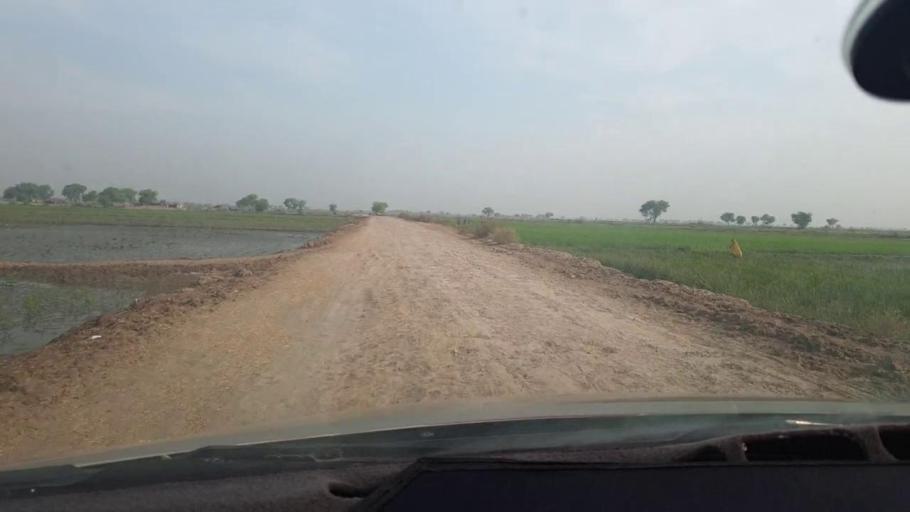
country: PK
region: Balochistan
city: Jhatpat
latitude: 28.3541
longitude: 68.4091
